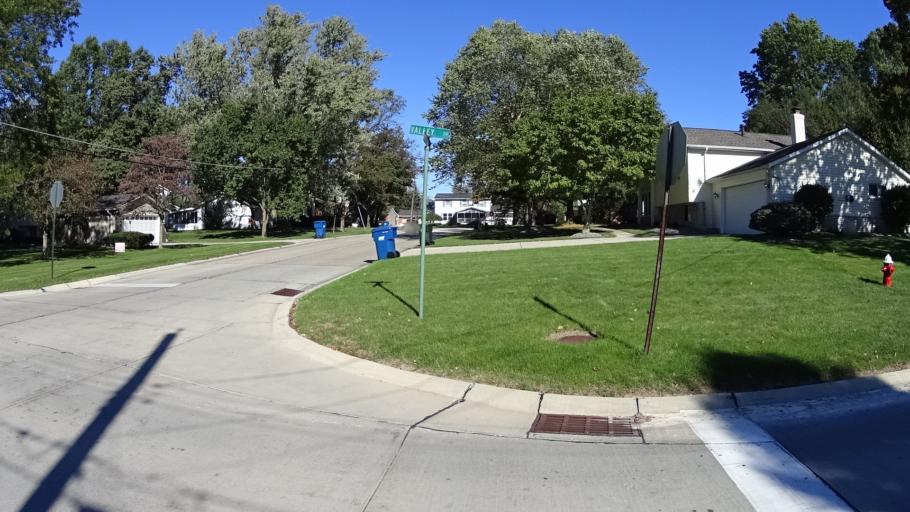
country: US
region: Ohio
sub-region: Lorain County
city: Amherst
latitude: 41.3911
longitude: -82.2433
